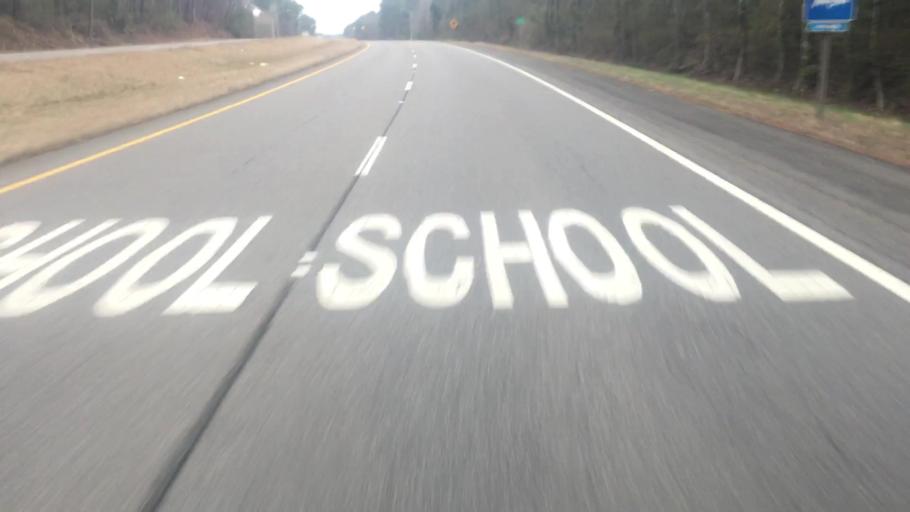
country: US
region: Alabama
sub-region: Walker County
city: Cordova
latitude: 33.8213
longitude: -87.1849
